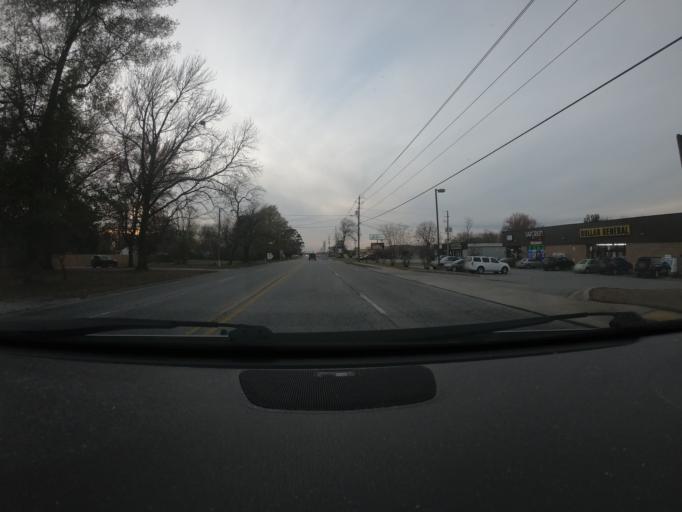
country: US
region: Arkansas
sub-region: Benton County
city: Rogers
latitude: 36.3339
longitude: -94.1395
